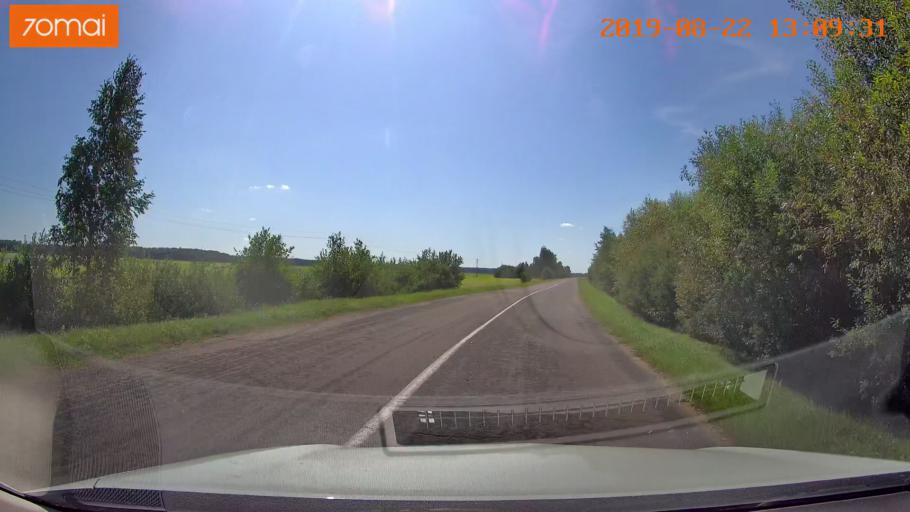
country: BY
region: Minsk
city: Prawdzinski
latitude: 53.3090
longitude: 27.8511
